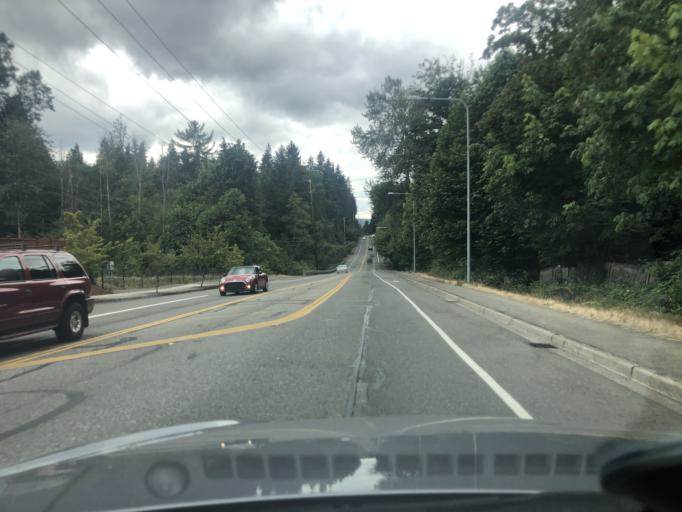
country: US
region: Washington
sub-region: King County
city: Lea Hill
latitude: 47.3226
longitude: -122.1818
